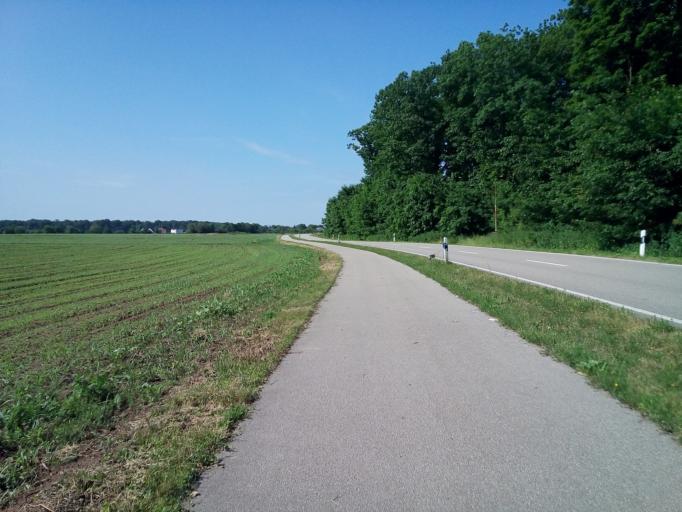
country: DE
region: Baden-Wuerttemberg
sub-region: Freiburg Region
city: Rheinau
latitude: 48.6163
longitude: 7.9128
